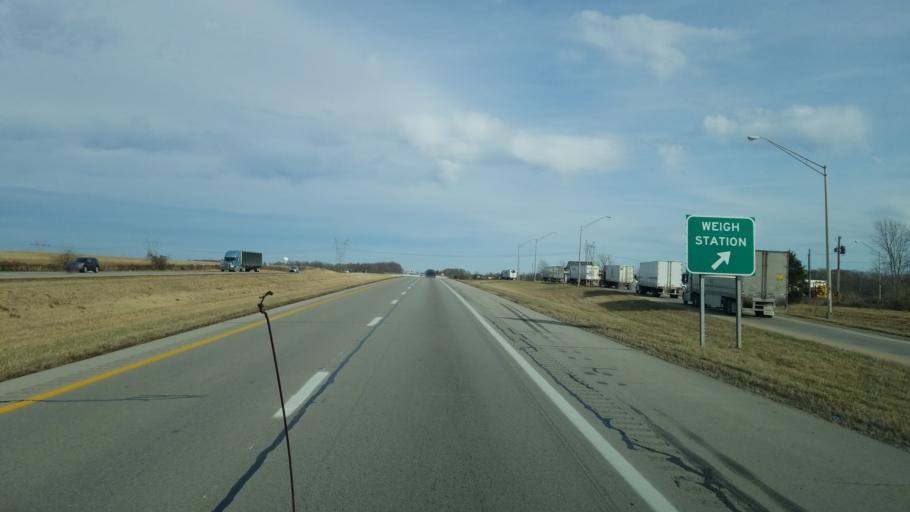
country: US
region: Ohio
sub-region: Clinton County
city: Wilmington
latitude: 39.5065
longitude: -83.8792
